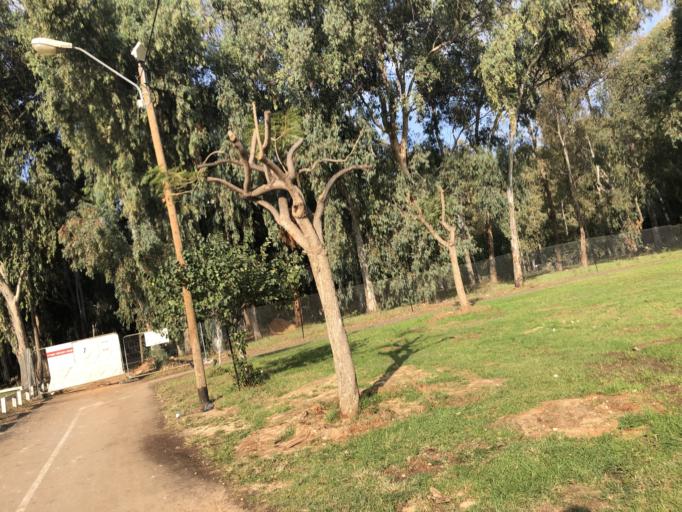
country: IL
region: Tel Aviv
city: Giv`atayim
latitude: 32.0469
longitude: 34.8211
